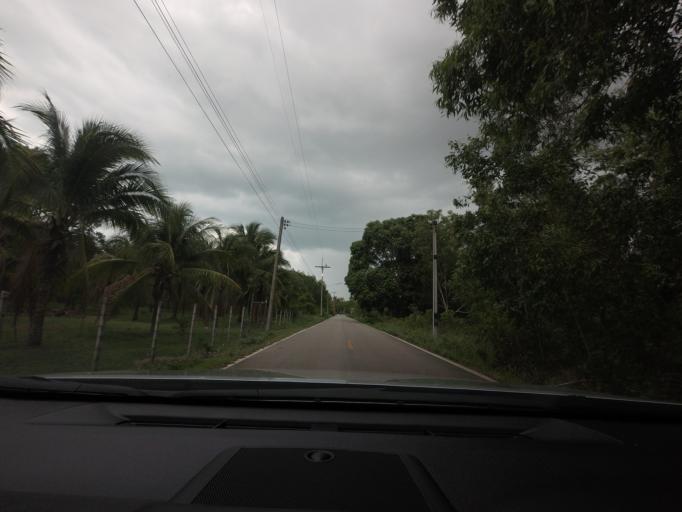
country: TH
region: Songkhla
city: Chana
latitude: 6.9538
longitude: 100.8383
